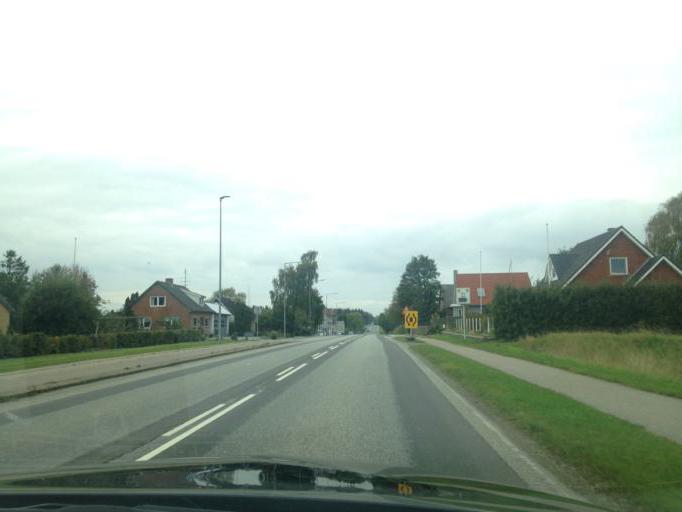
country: DK
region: South Denmark
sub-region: Kolding Kommune
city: Christiansfeld
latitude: 55.3941
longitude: 9.4794
